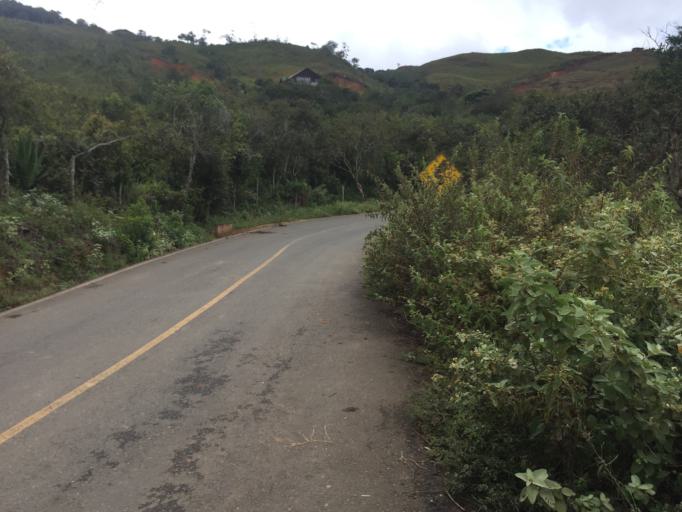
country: CO
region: Valle del Cauca
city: Dagua
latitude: 3.6893
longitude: -76.5930
